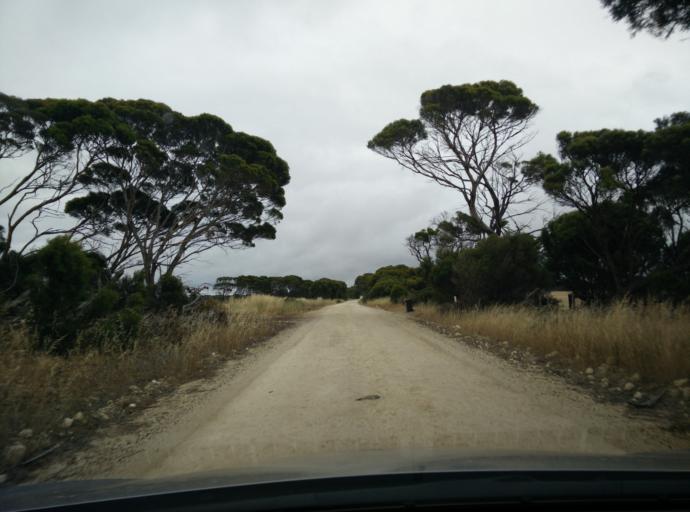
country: AU
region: South Australia
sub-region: Kangaroo Island
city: Kingscote
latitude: -35.8690
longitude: 137.5273
